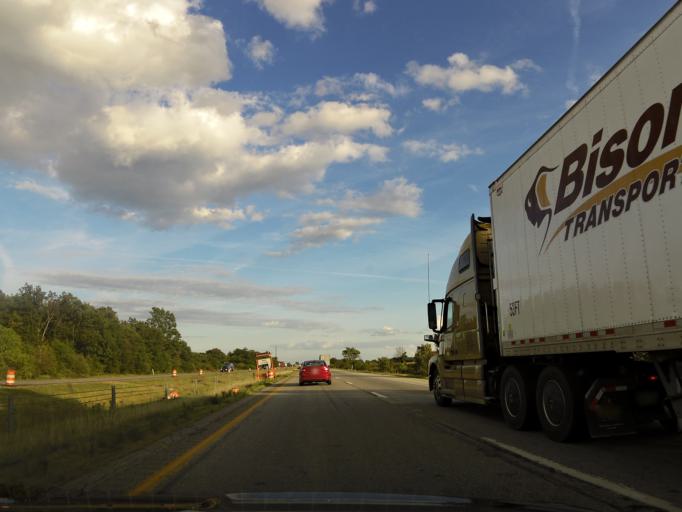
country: US
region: Indiana
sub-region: Boone County
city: Thorntown
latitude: 40.2102
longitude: -86.5912
